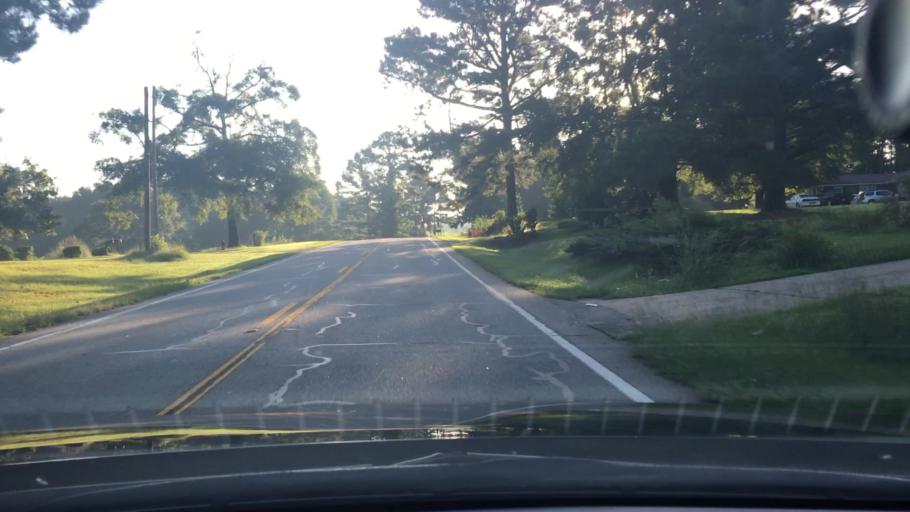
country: US
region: Georgia
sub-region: Fayette County
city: Peachtree City
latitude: 33.3762
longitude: -84.6859
